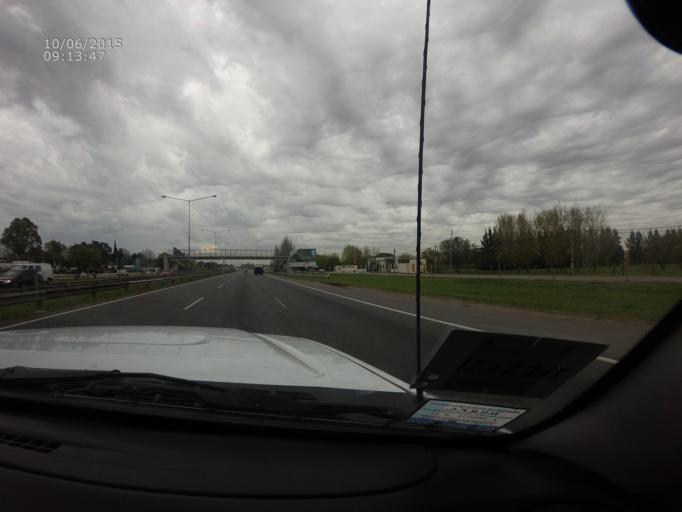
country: AR
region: Buenos Aires
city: Belen de Escobar
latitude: -34.3348
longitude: -58.8251
